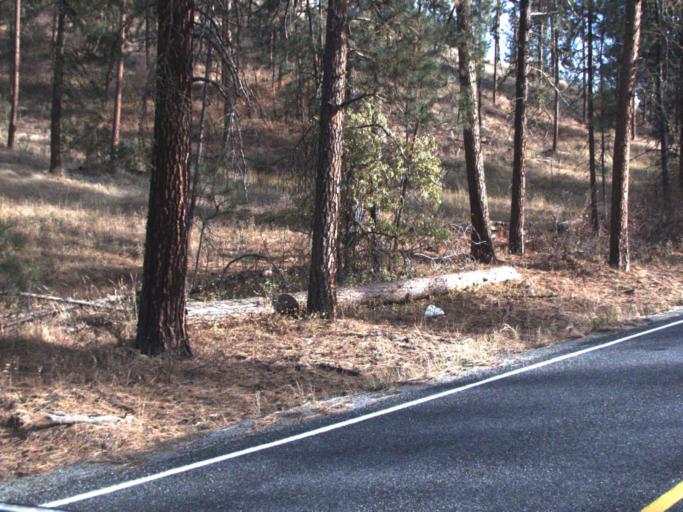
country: US
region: Washington
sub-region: Stevens County
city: Kettle Falls
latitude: 48.2932
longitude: -118.1430
